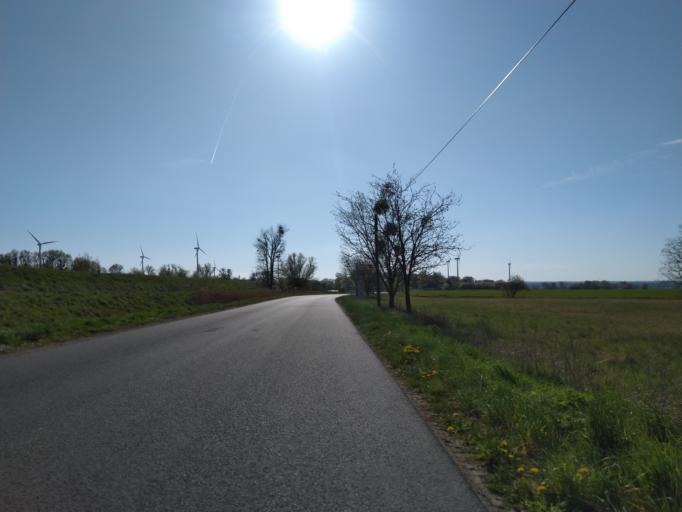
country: DE
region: Brandenburg
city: Bliesdorf
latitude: 52.7112
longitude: 14.1963
